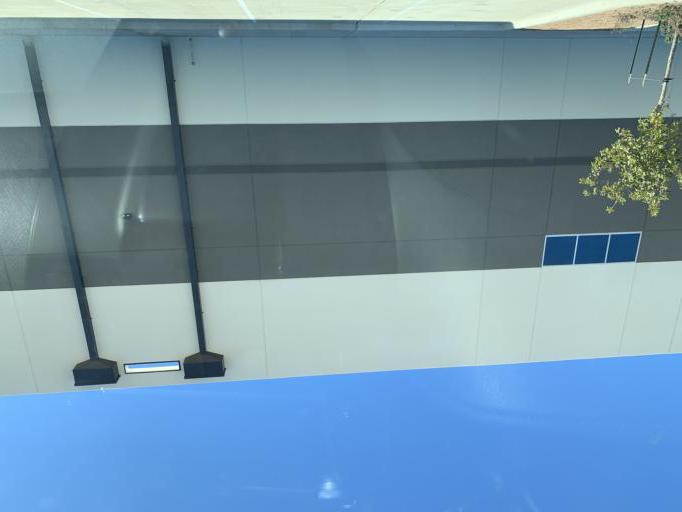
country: US
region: Texas
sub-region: Williamson County
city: Hutto
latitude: 30.5489
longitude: -97.5689
